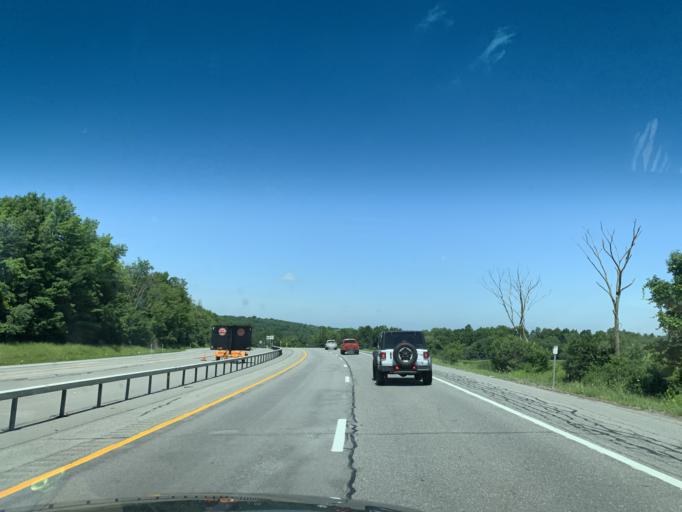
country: US
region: New York
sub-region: Oneida County
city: Chadwicks
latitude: 43.0305
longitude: -75.2665
